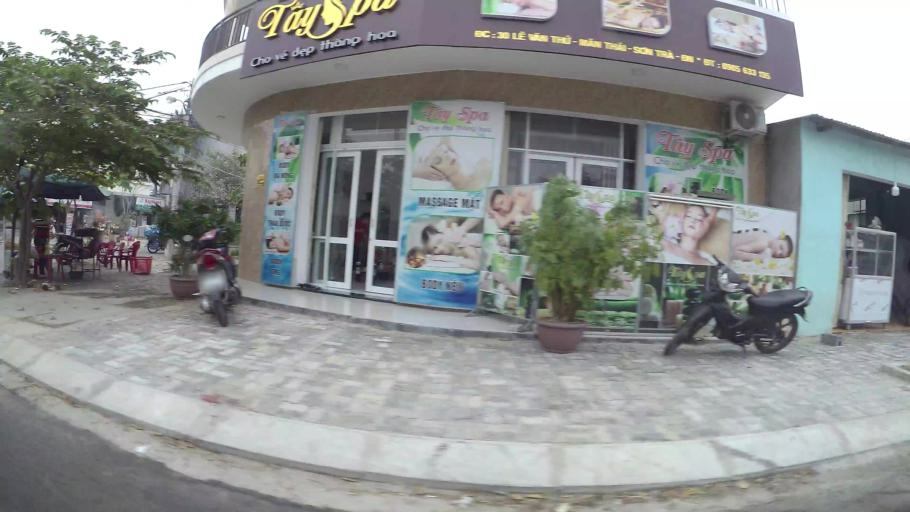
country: VN
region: Da Nang
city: Son Tra
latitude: 16.0853
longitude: 108.2424
